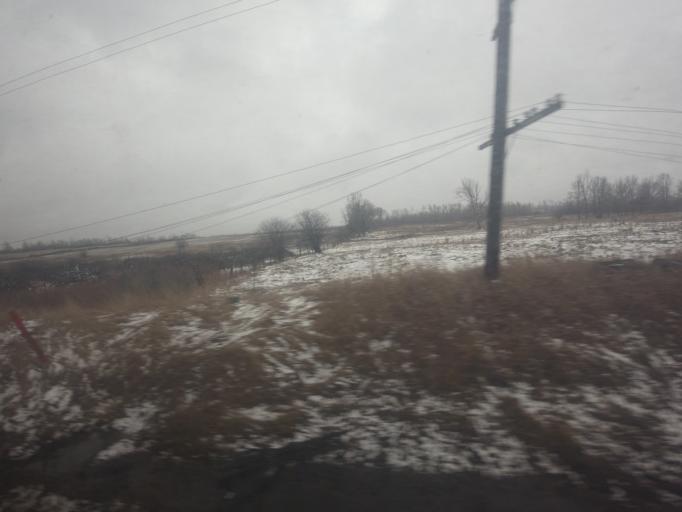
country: CA
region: Ontario
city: Deseronto
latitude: 44.2216
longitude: -77.1391
